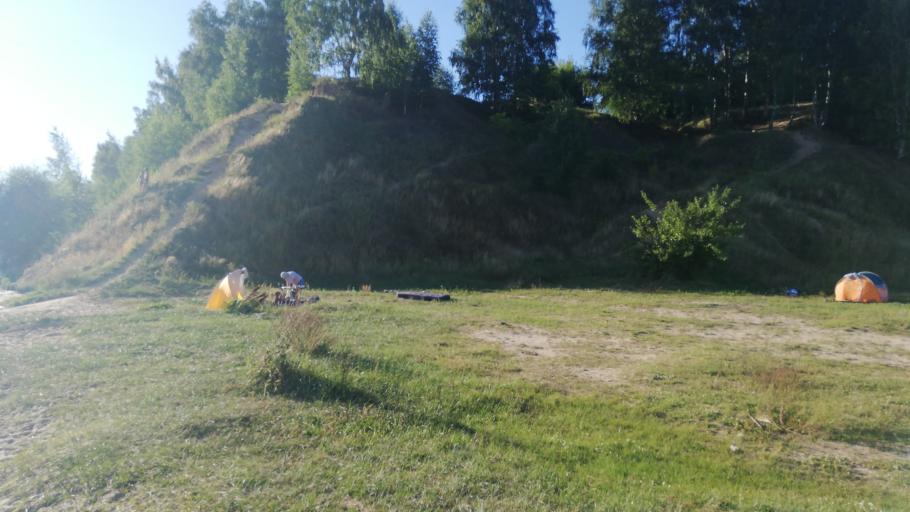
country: RU
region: Nizjnij Novgorod
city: Zavolzh'ye
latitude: 56.6872
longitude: 43.4225
